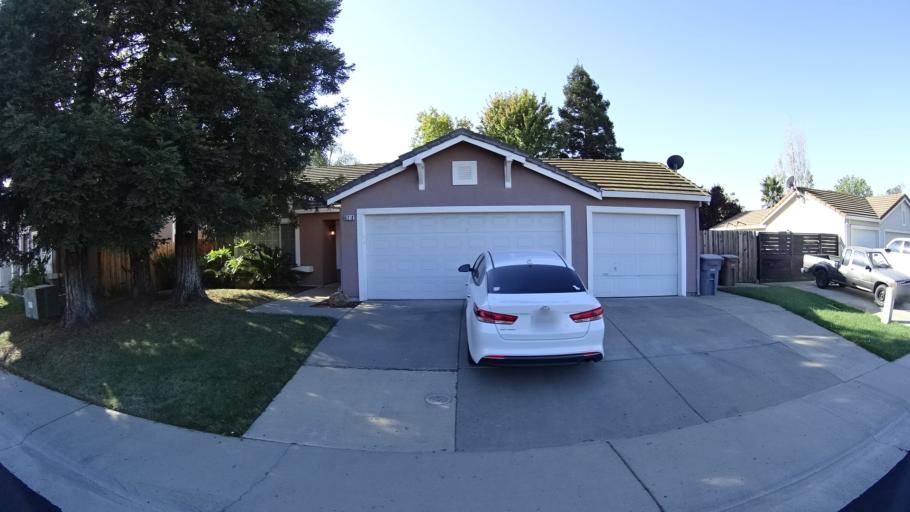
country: US
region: California
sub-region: Sacramento County
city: Laguna
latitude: 38.4251
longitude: -121.4438
